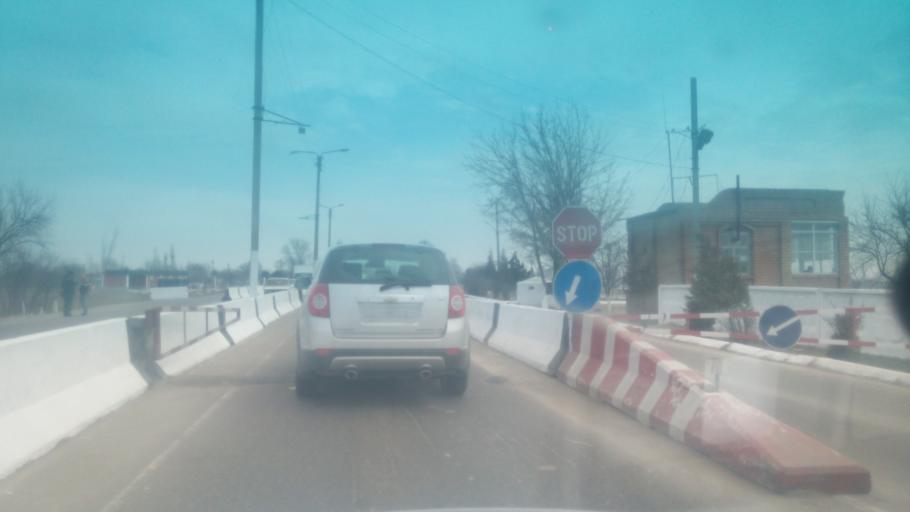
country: KZ
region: Ongtustik Qazaqstan
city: Myrzakent
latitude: 40.5034
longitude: 68.5249
